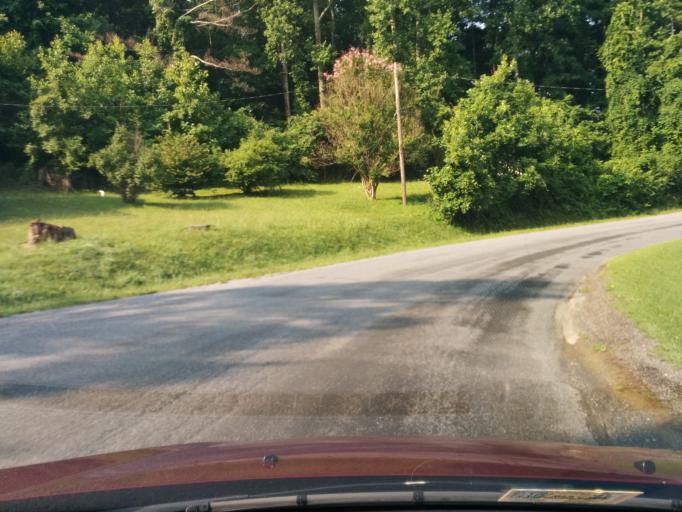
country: US
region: Virginia
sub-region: City of Lexington
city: Lexington
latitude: 37.7900
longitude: -79.5017
